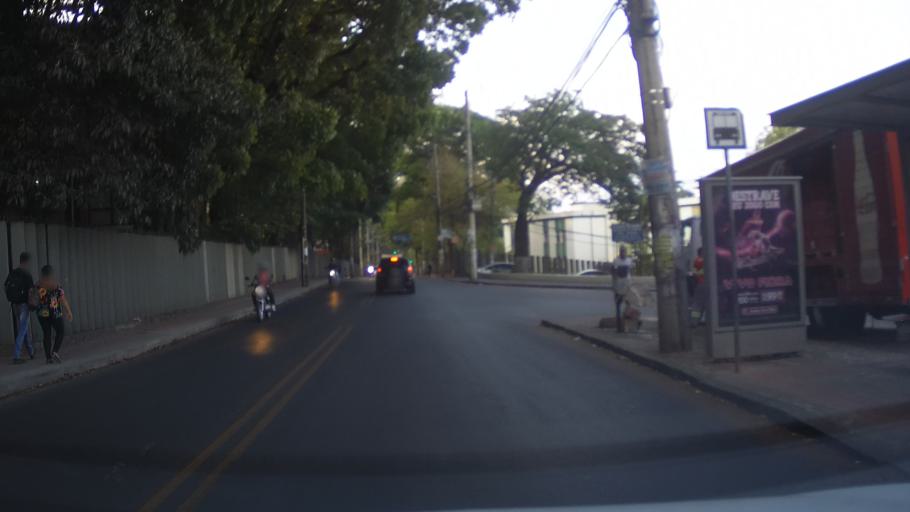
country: BR
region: Minas Gerais
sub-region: Belo Horizonte
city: Belo Horizonte
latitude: -19.8974
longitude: -43.9117
